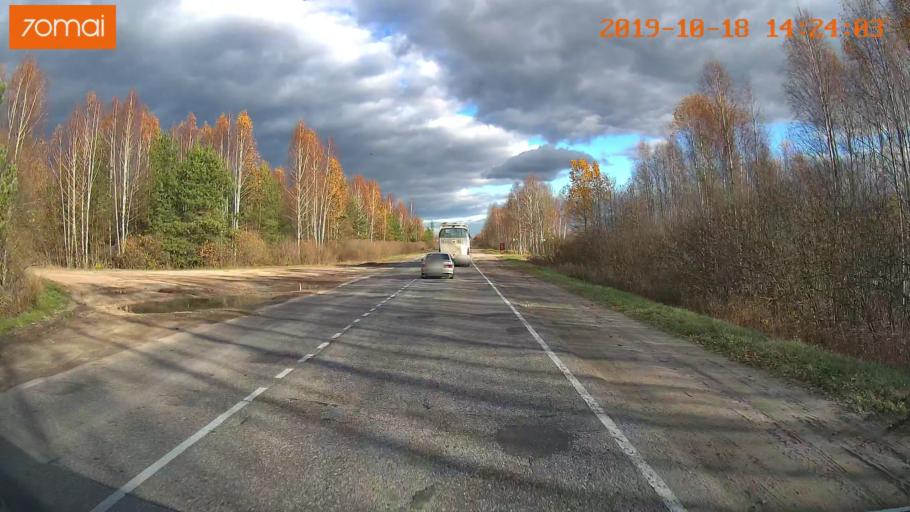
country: RU
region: Rjazan
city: Tuma
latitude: 55.1475
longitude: 40.4934
